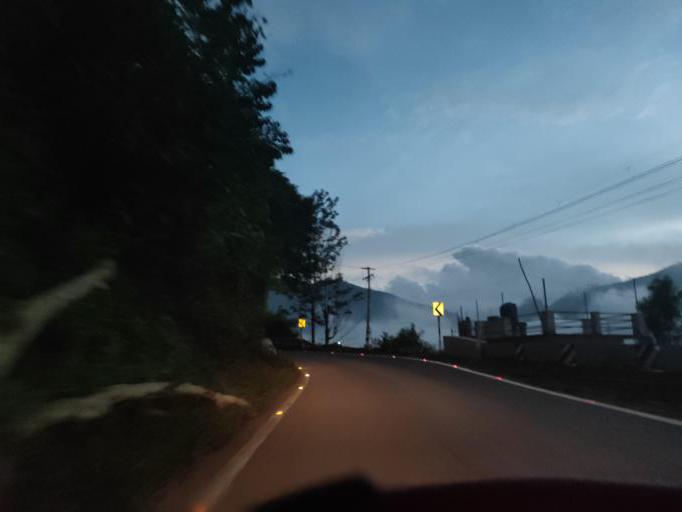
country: IN
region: Tamil Nadu
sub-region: Dindigul
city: Kodaikanal
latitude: 10.2772
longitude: 77.5334
